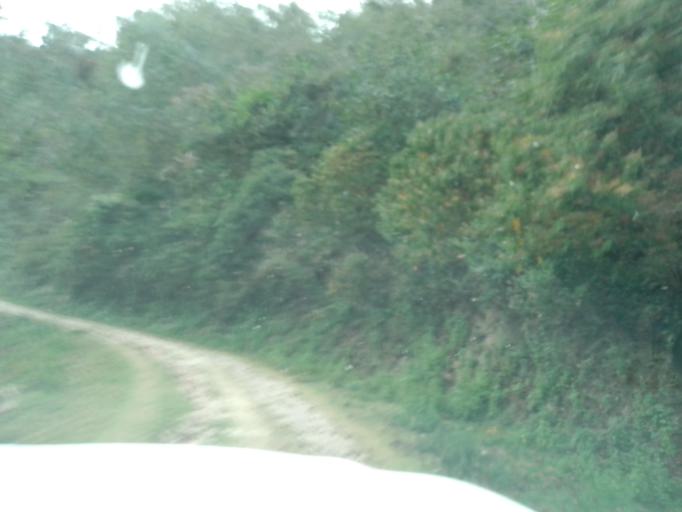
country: MX
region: Chiapas
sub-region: Cacahoatan
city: Benito Juarez
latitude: 15.2072
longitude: -92.2221
